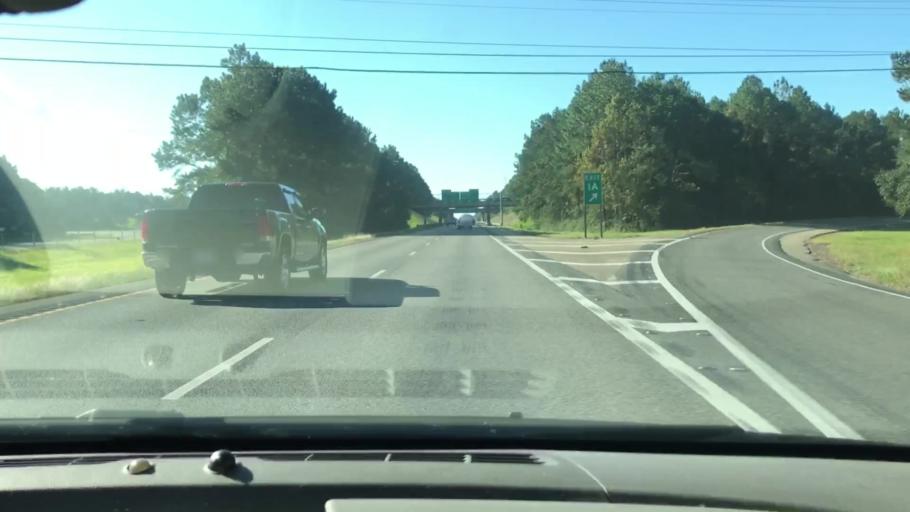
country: US
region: Louisiana
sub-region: Saint Tammany Parish
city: Slidell
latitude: 30.3102
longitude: -89.7402
